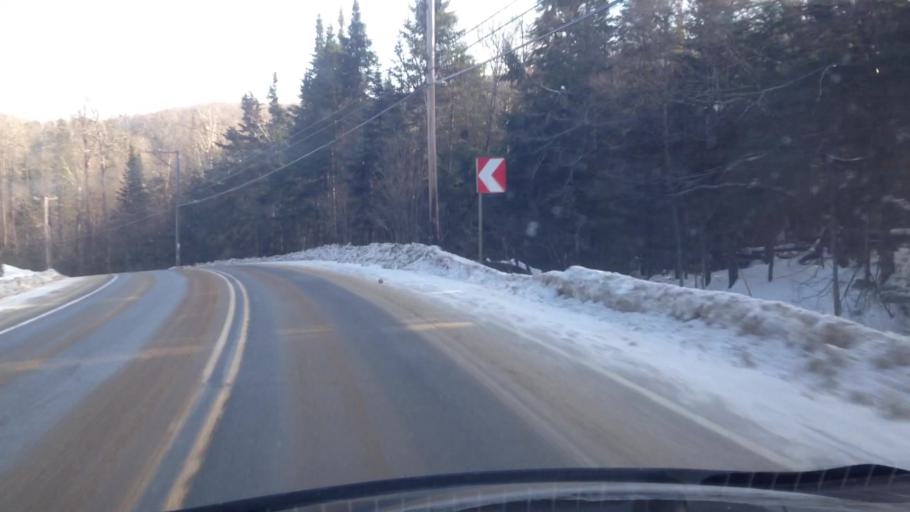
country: CA
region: Quebec
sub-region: Laurentides
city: Sainte-Agathe-des-Monts
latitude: 45.9108
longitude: -74.3557
